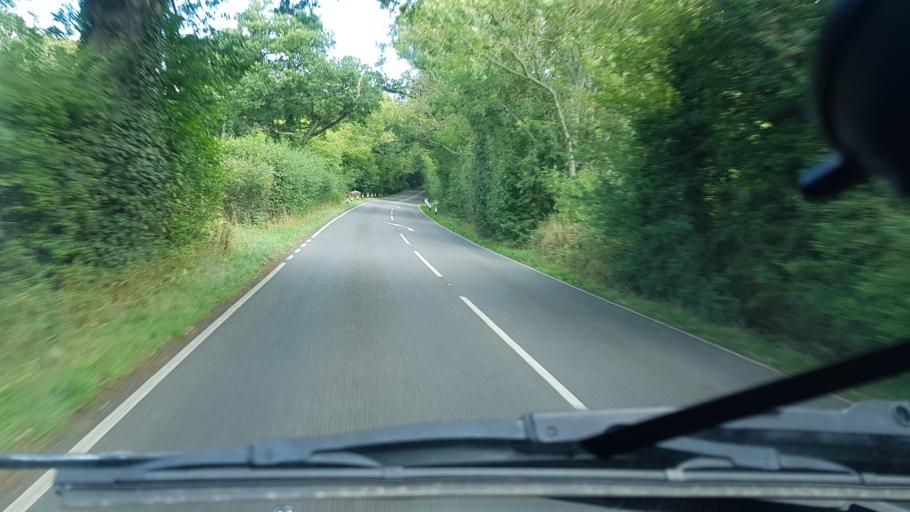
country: GB
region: England
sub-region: Surrey
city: Ockley
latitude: 51.1026
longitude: -0.3740
